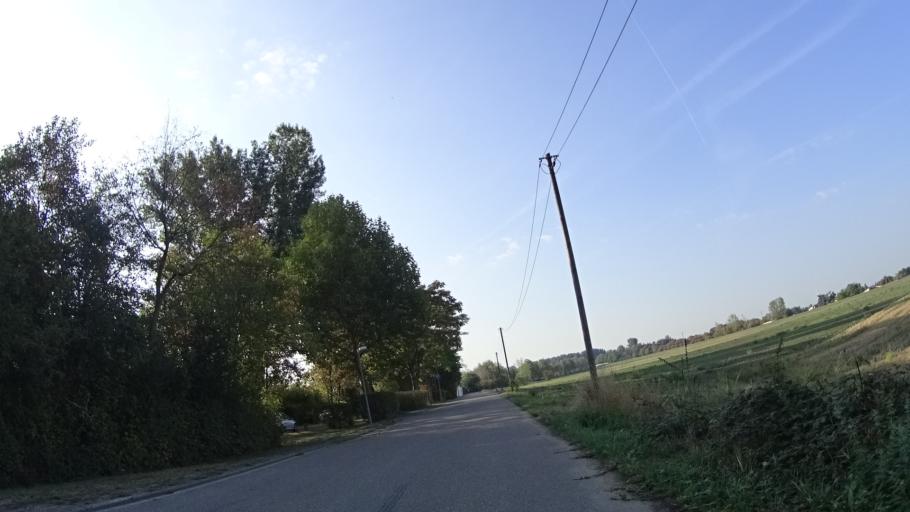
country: DE
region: Baden-Wuerttemberg
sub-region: Karlsruhe Region
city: Ketsch
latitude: 49.3623
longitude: 8.5194
